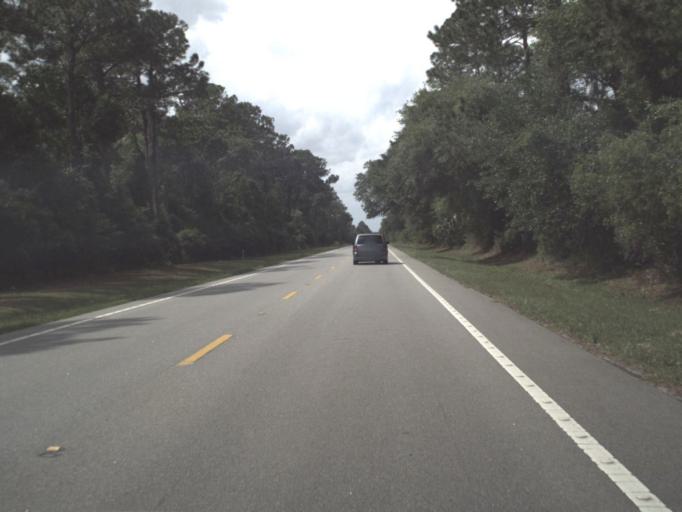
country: US
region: Florida
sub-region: Putnam County
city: Crescent City
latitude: 29.5010
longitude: -81.4862
